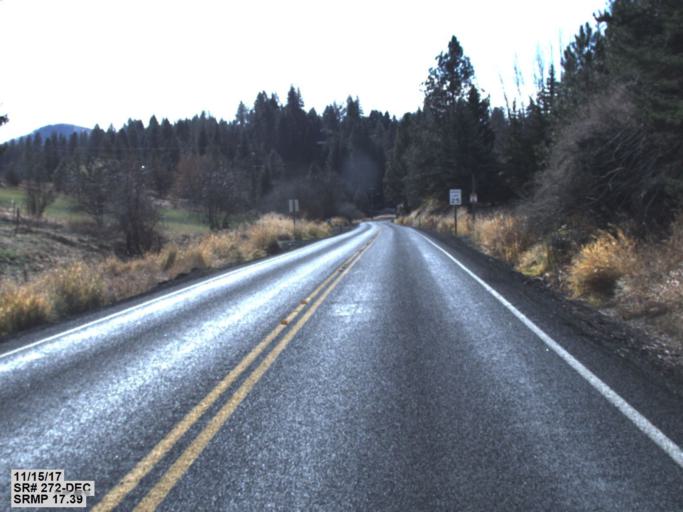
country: US
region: Idaho
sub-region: Latah County
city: Moscow
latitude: 46.9138
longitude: -117.0672
